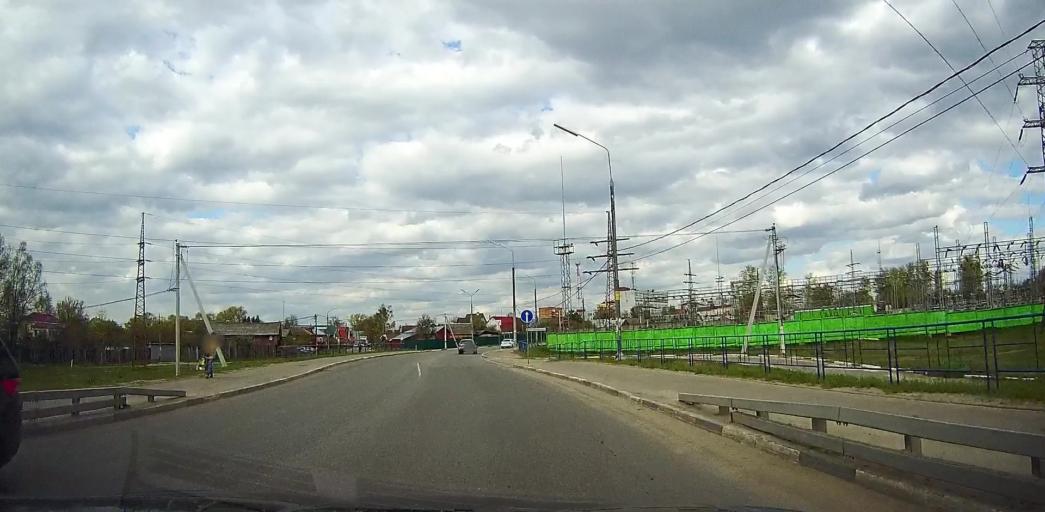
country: RU
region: Moskovskaya
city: Pavlovskiy Posad
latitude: 55.7738
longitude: 38.6449
